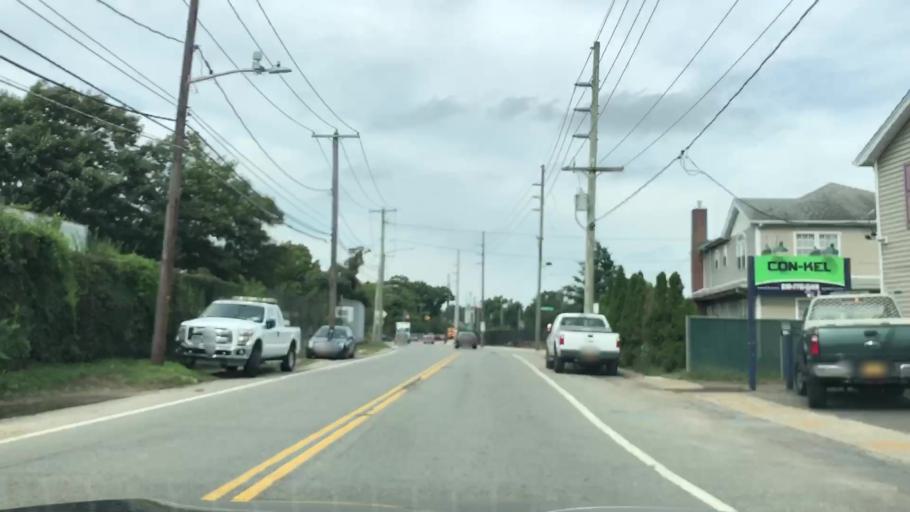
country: US
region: New York
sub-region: Nassau County
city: South Floral Park
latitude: 40.7133
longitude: -73.7082
